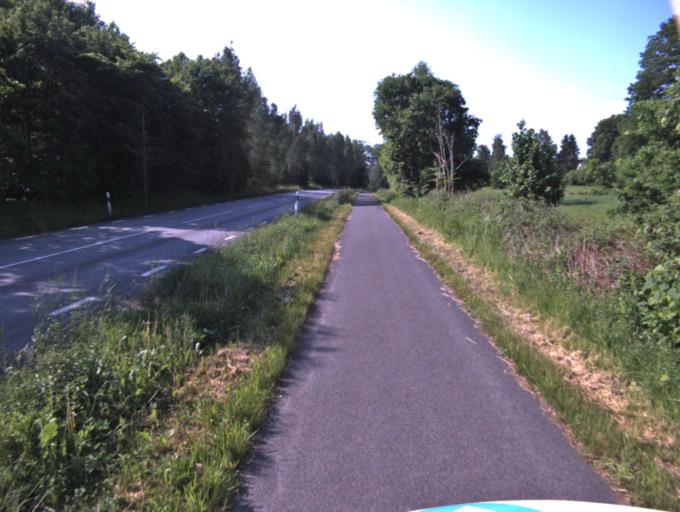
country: SE
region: Skane
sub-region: Kristianstads Kommun
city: Tollarp
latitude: 56.1694
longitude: 14.2821
